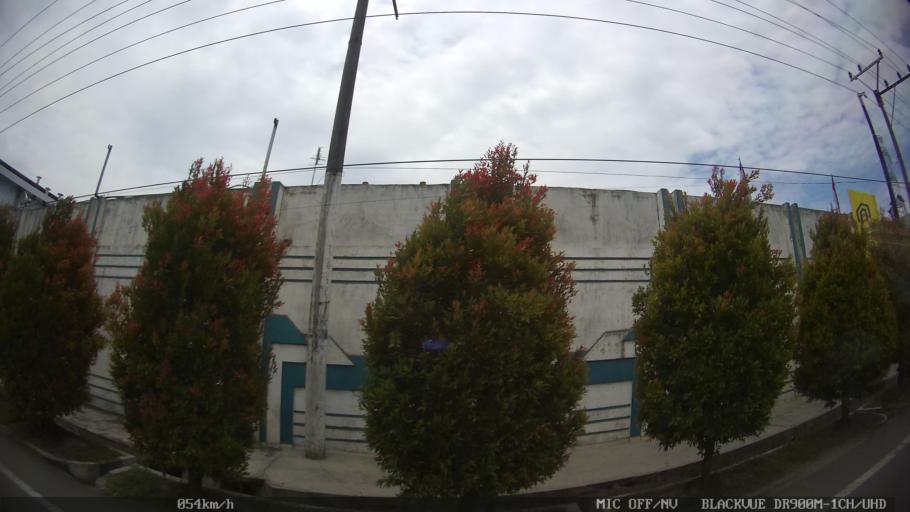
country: ID
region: North Sumatra
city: Sunggal
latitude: 3.5995
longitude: 98.5866
